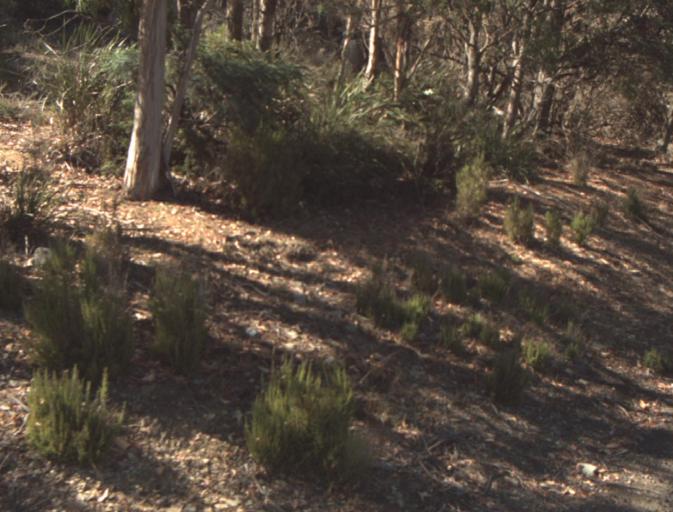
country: AU
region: Tasmania
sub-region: Launceston
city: Newstead
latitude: -41.2992
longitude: 147.3351
